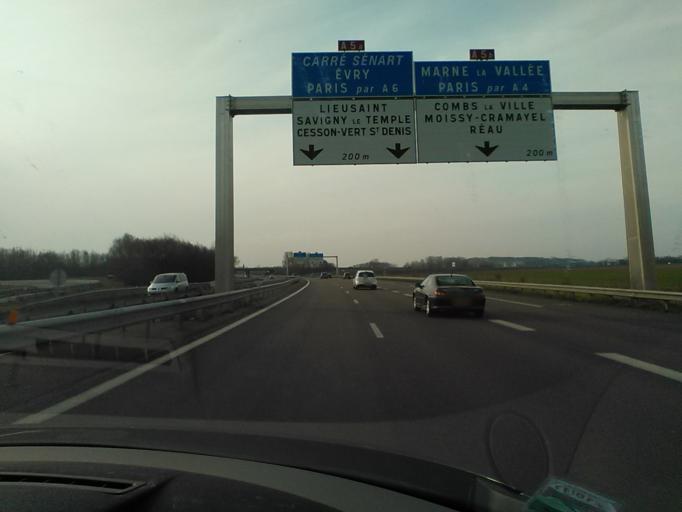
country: FR
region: Ile-de-France
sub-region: Departement de Seine-et-Marne
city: Voisenon
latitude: 48.5933
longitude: 2.6414
